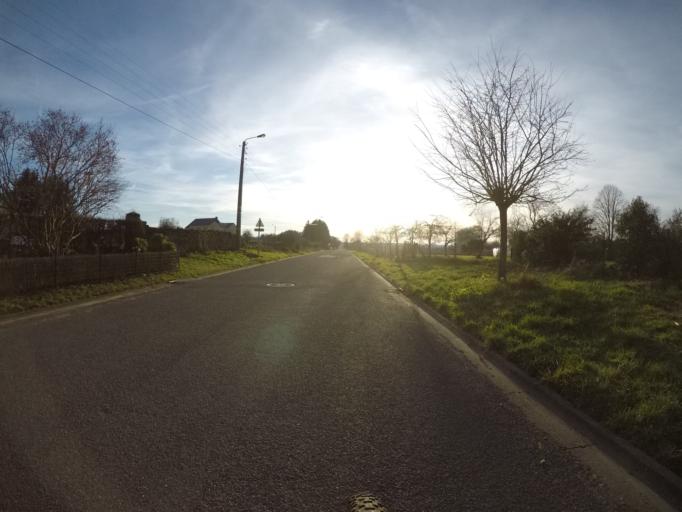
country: BE
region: Wallonia
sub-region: Province du Luxembourg
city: Tintigny
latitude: 49.6749
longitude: 5.4703
